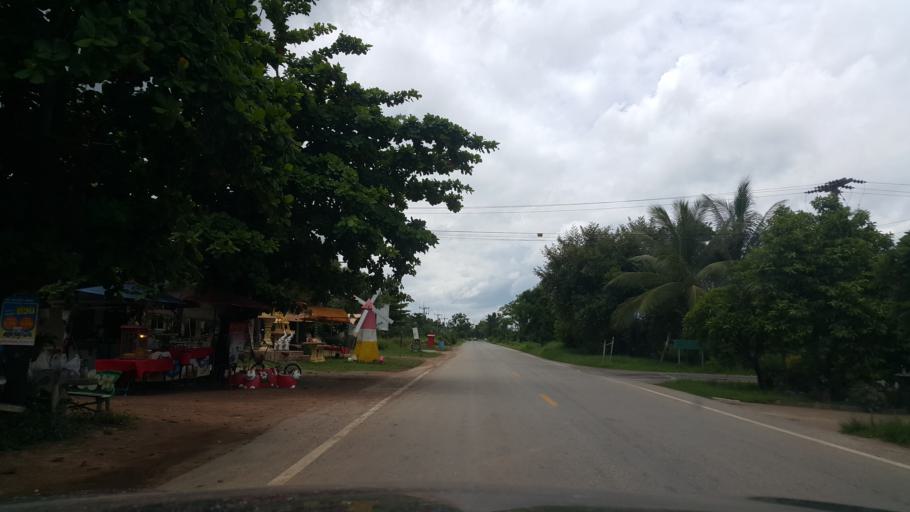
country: TH
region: Sukhothai
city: Kong Krailat
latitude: 16.9105
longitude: 99.8779
